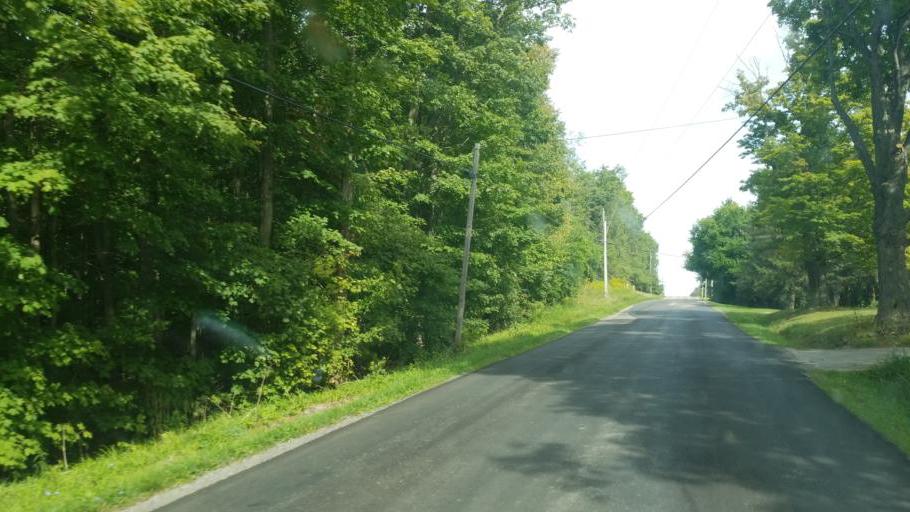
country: US
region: Ohio
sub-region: Knox County
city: Mount Vernon
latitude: 40.3830
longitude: -82.5400
